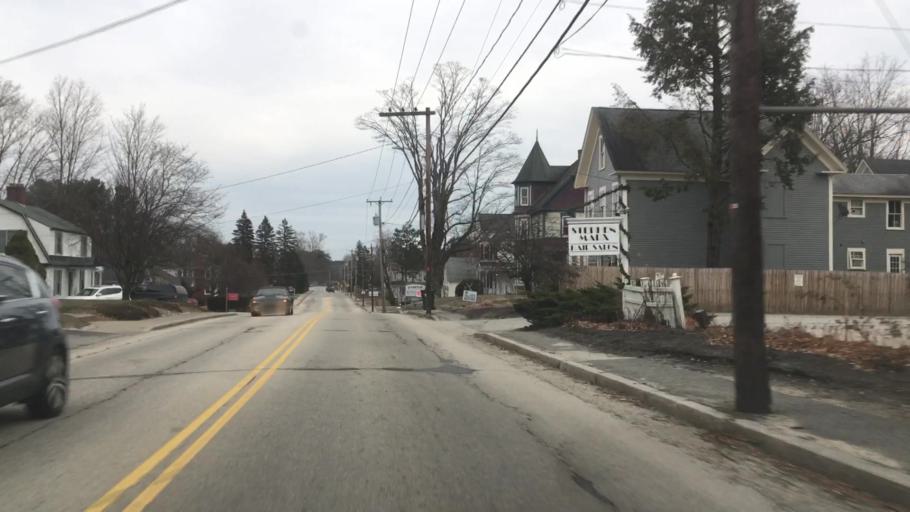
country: US
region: New Hampshire
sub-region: Hillsborough County
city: Milford
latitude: 42.8317
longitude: -71.6410
